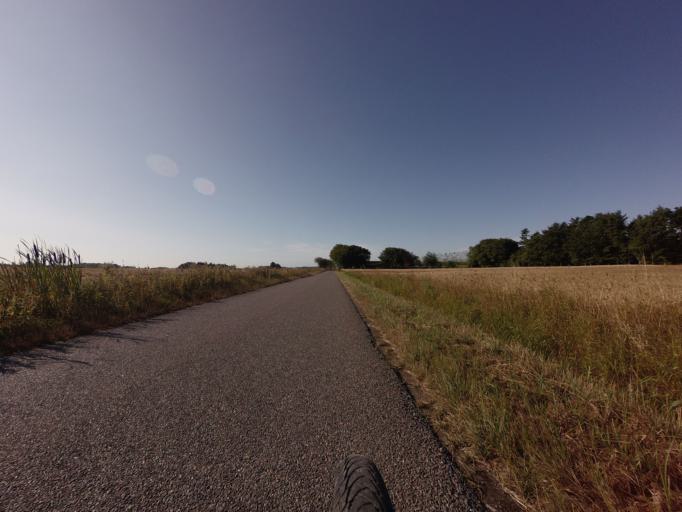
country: DK
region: North Denmark
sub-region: Hjorring Kommune
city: Vra
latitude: 57.3812
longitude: 9.9567
